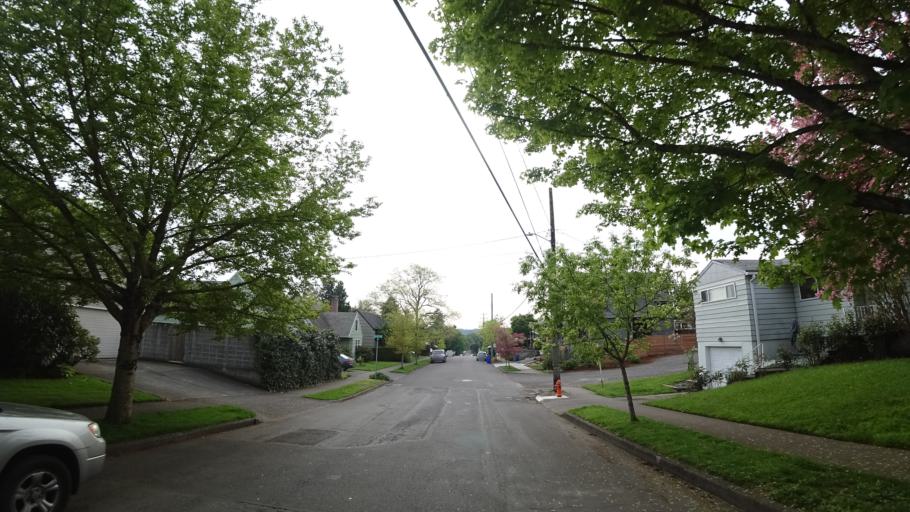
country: US
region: Oregon
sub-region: Clackamas County
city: Milwaukie
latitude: 45.4705
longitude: -122.6206
